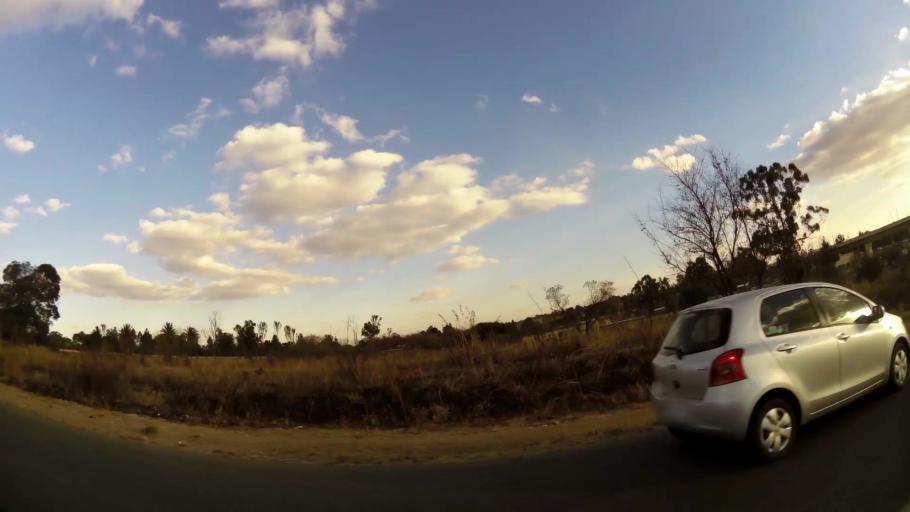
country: ZA
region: Gauteng
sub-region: City of Johannesburg Metropolitan Municipality
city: Midrand
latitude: -25.9554
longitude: 28.1437
